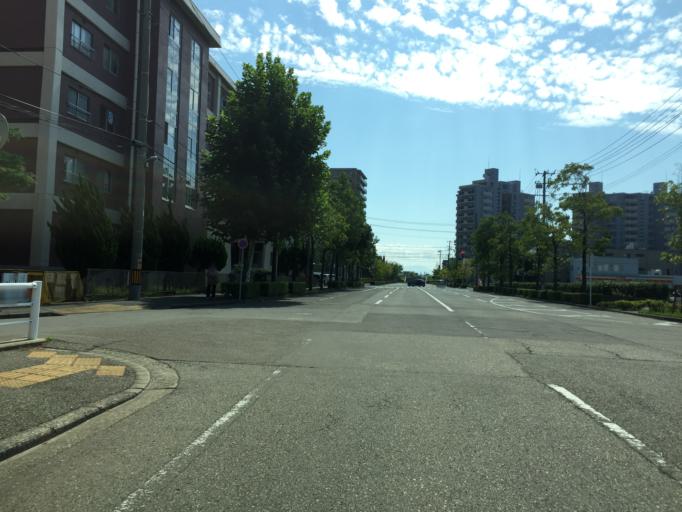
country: JP
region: Niigata
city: Niigata-shi
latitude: 37.9117
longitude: 139.0316
